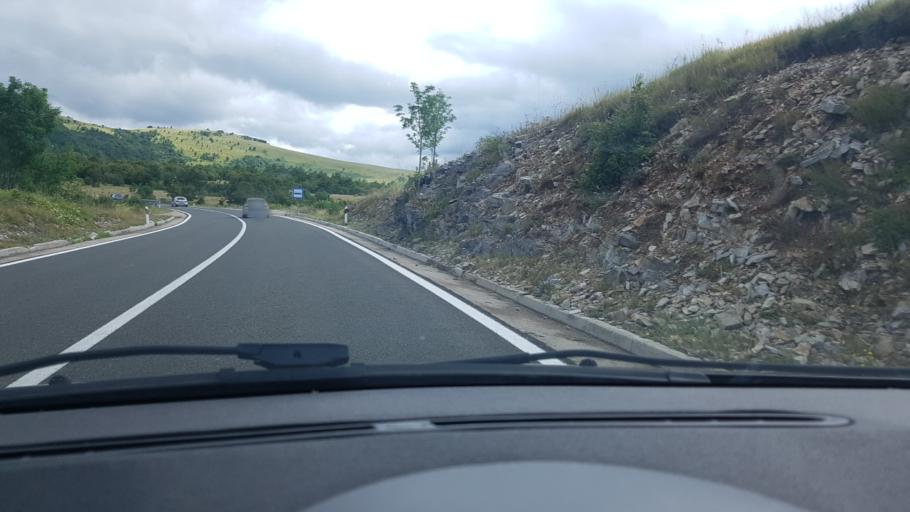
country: HR
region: Zadarska
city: Gracac
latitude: 44.4247
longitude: 15.8754
